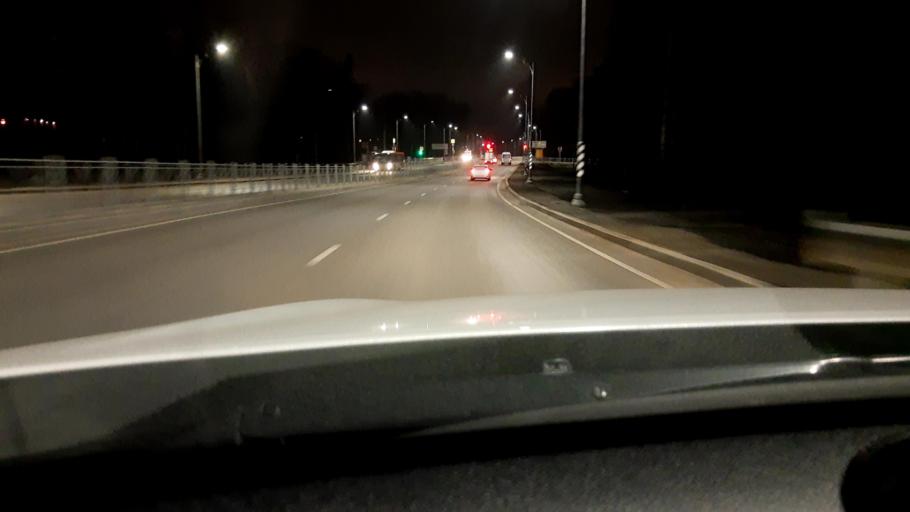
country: RU
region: Moskovskaya
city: Reutov
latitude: 55.7590
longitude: 37.8843
